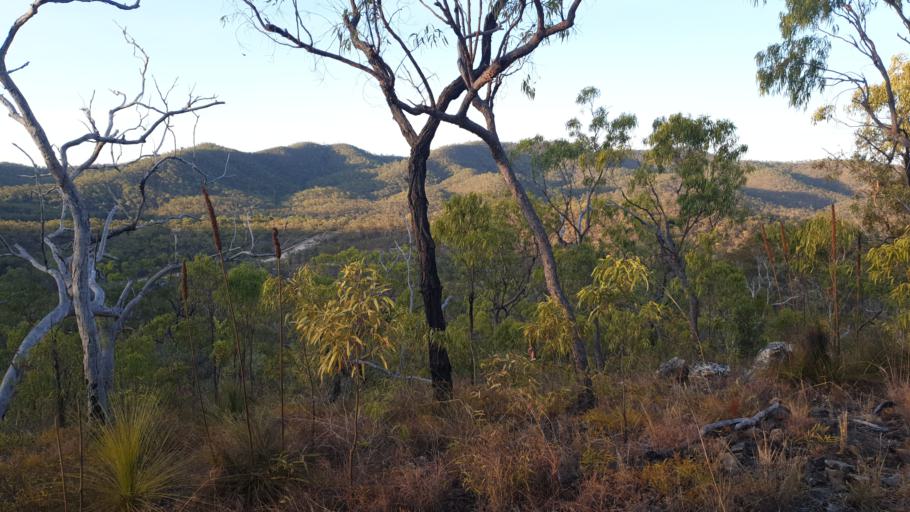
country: AU
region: Queensland
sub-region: Tablelands
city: Atherton
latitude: -17.4014
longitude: 145.2262
